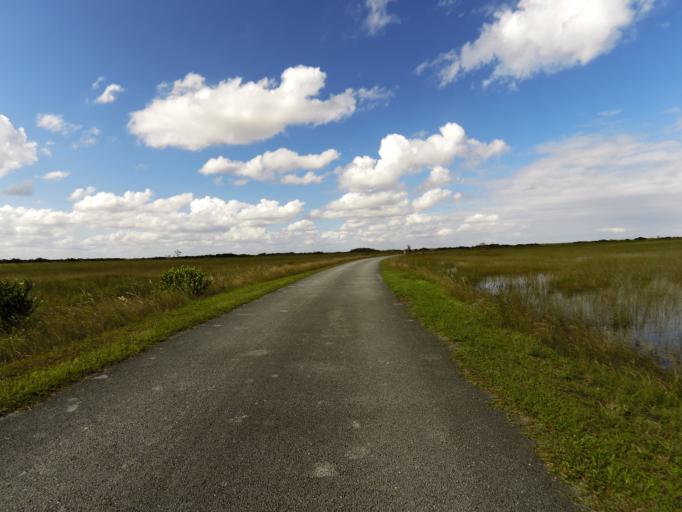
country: US
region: Florida
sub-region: Miami-Dade County
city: The Hammocks
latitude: 25.7336
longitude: -80.7598
